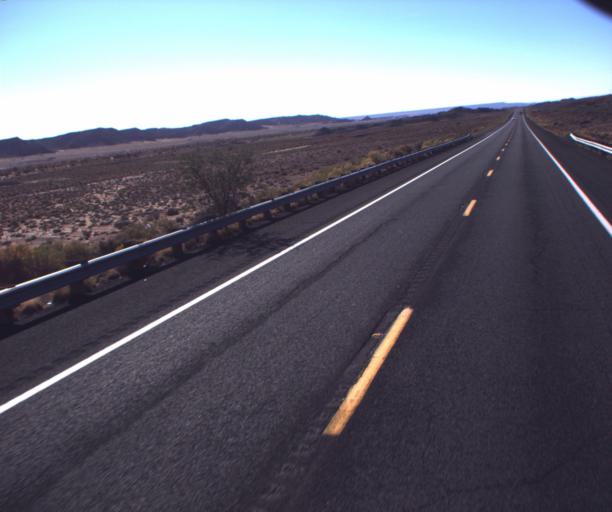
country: US
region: Arizona
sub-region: Coconino County
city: Tuba City
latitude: 36.1441
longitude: -111.3968
